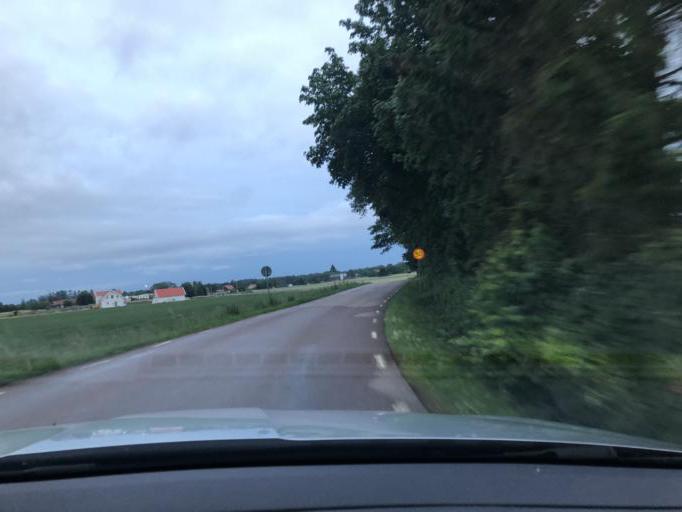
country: SE
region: OEstergoetland
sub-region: Vadstena Kommun
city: Herrestad
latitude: 58.2946
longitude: 14.7781
